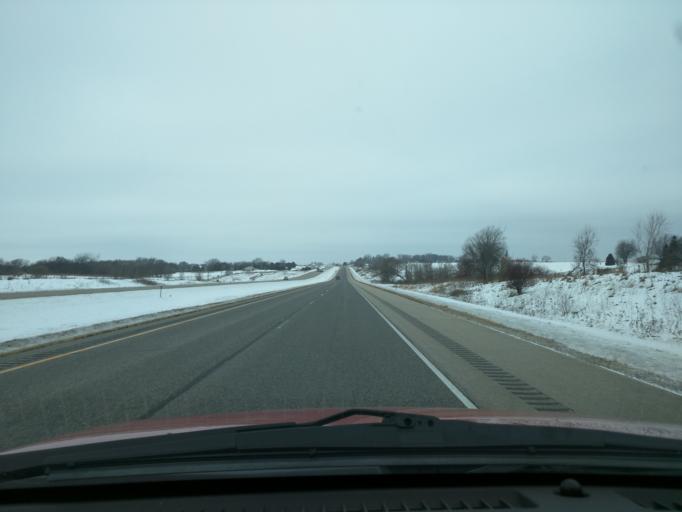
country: US
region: Minnesota
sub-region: Winona County
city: Winona
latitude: 43.9319
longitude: -91.6213
